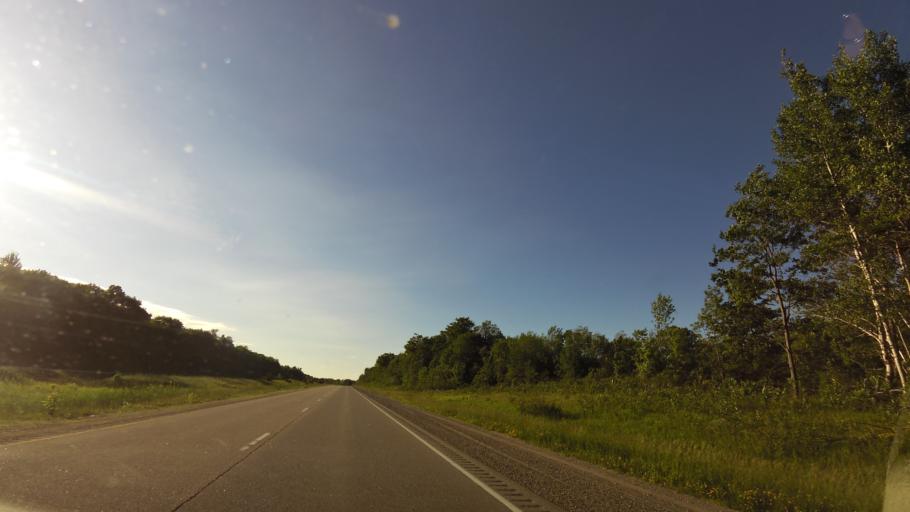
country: CA
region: Ontario
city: Midland
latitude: 44.7268
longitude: -79.6771
